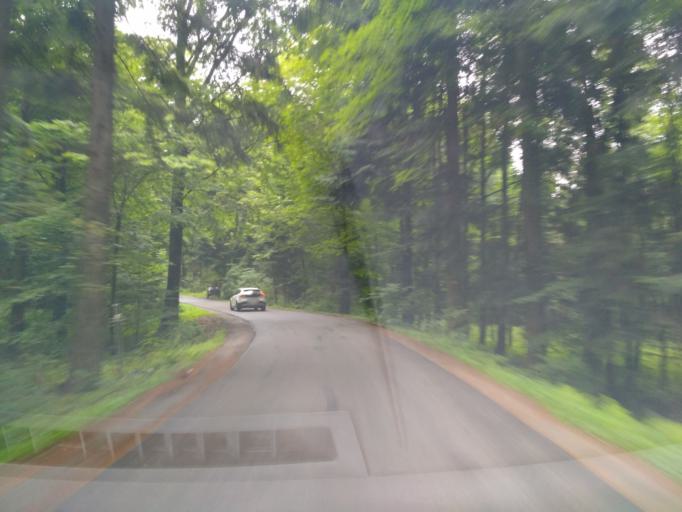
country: PL
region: Subcarpathian Voivodeship
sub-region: Powiat strzyzowski
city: Strzyzow
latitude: 49.9002
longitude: 21.7853
